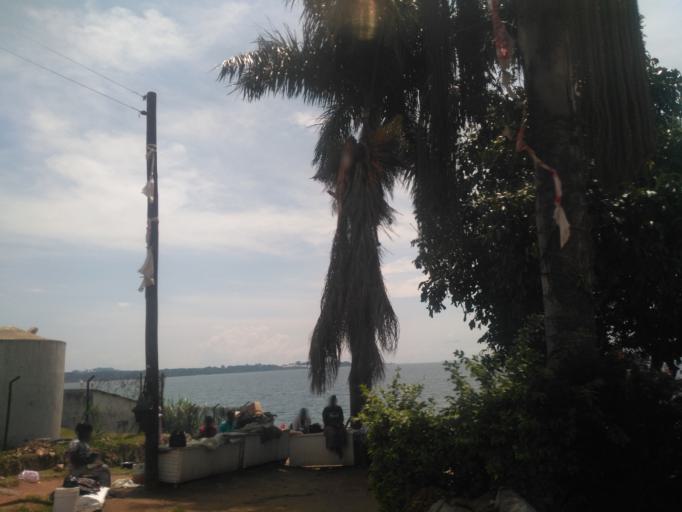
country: UG
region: Central Region
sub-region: Wakiso District
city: Entebbe
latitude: 0.0717
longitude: 32.4840
